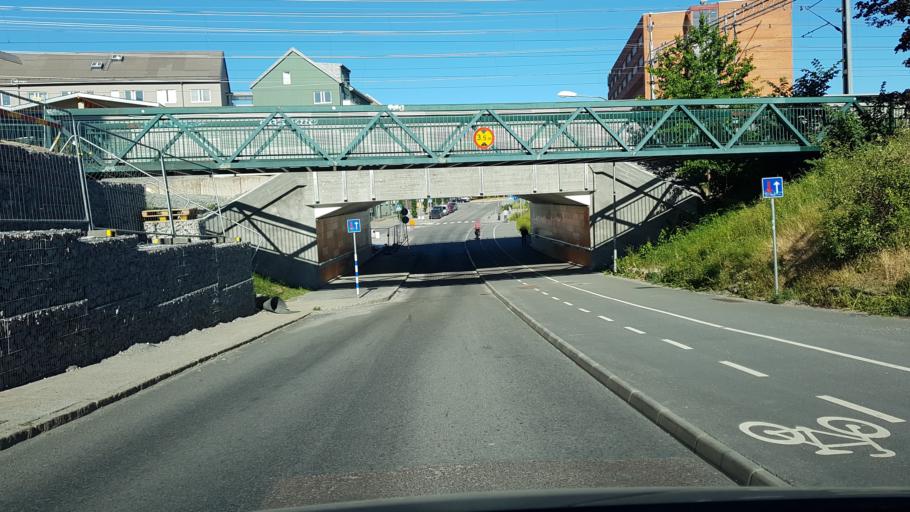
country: SE
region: Stockholm
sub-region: Jarfalla Kommun
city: Jakobsberg
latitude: 59.4179
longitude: 17.8331
